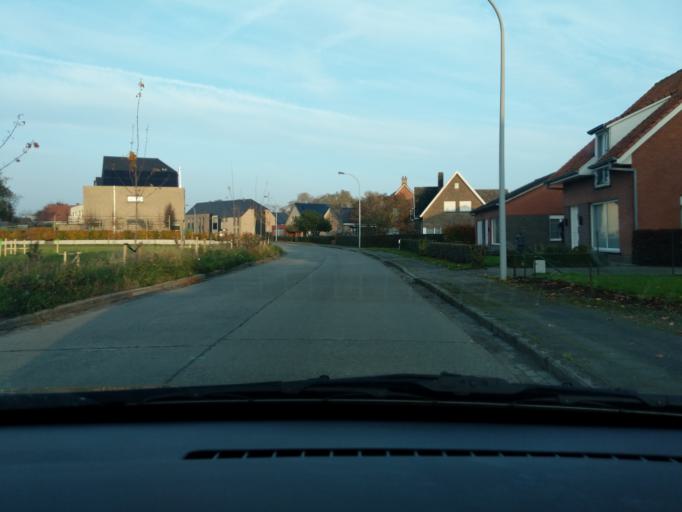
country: BE
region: Flanders
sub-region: Provincie Oost-Vlaanderen
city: Aalter
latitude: 51.0444
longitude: 3.4617
